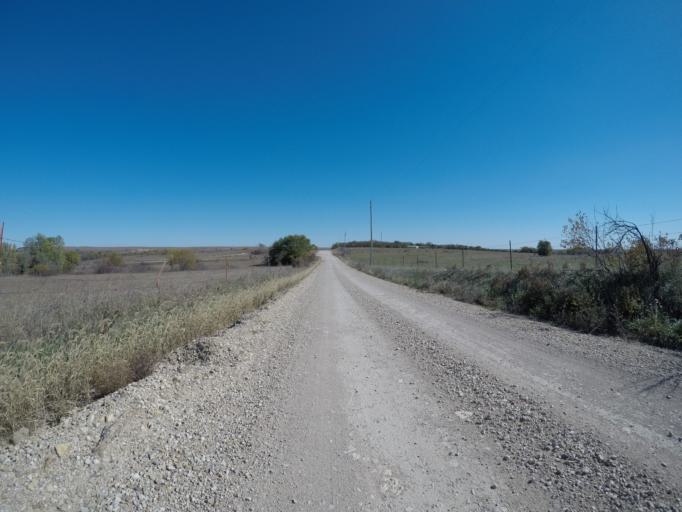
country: US
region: Kansas
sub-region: Wabaunsee County
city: Alma
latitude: 39.0580
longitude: -96.3551
